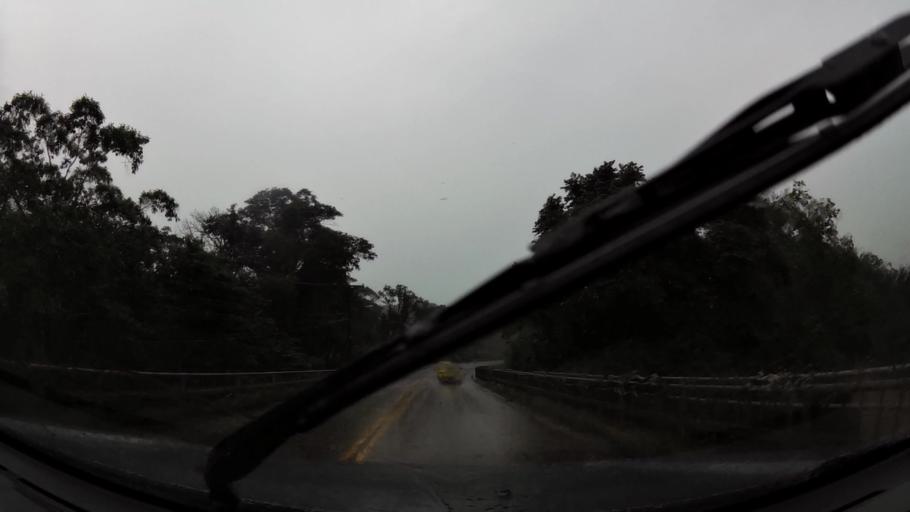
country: PA
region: Colon
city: Gatun
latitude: 9.2916
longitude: -79.7727
